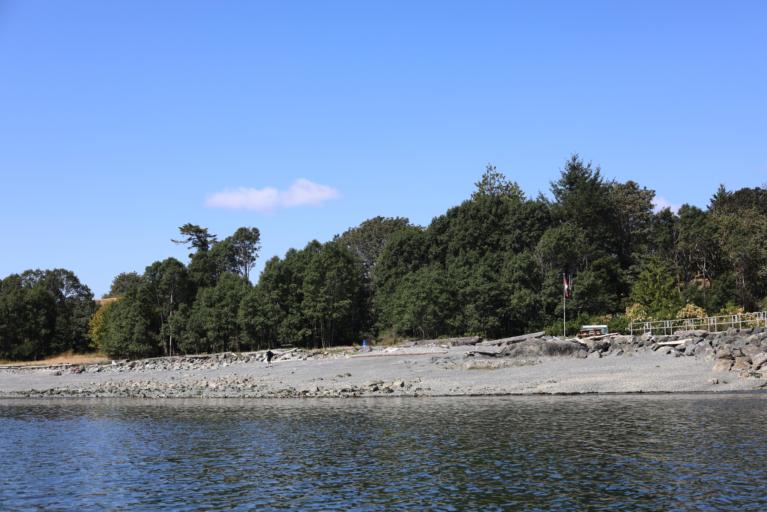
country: CA
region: British Columbia
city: Colwood
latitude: 48.4332
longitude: -123.4474
